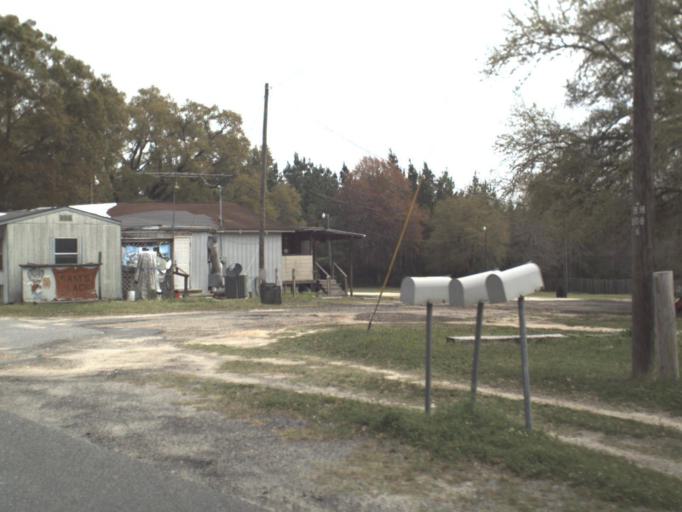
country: US
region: Florida
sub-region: Holmes County
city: Bonifay
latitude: 30.8504
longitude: -85.6667
